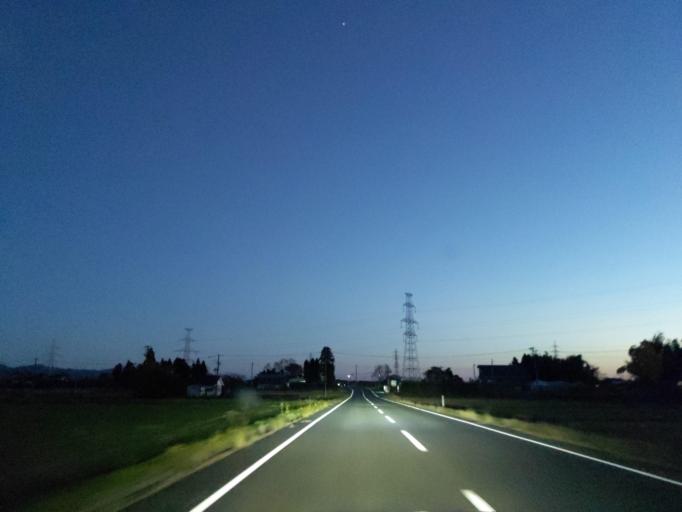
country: JP
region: Fukushima
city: Sukagawa
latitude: 37.3285
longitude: 140.3883
